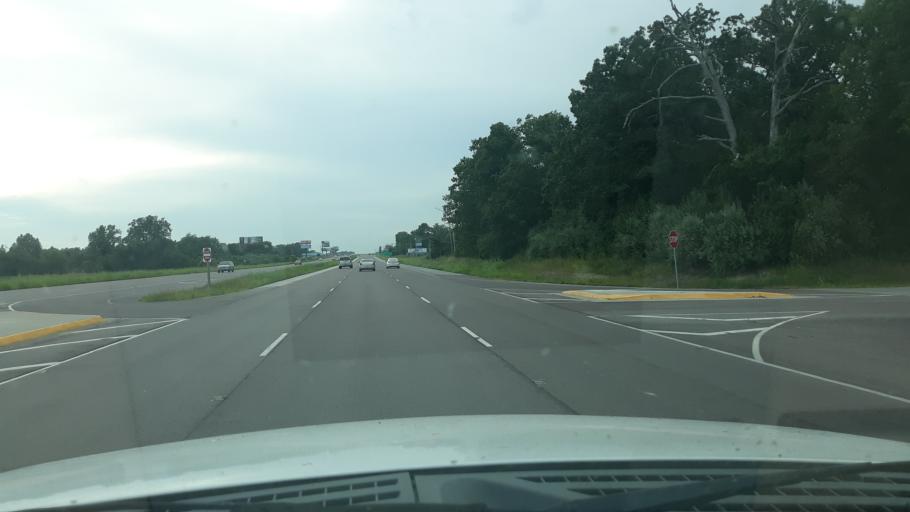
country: US
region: Illinois
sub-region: Williamson County
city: Energy
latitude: 37.7451
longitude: -89.0352
